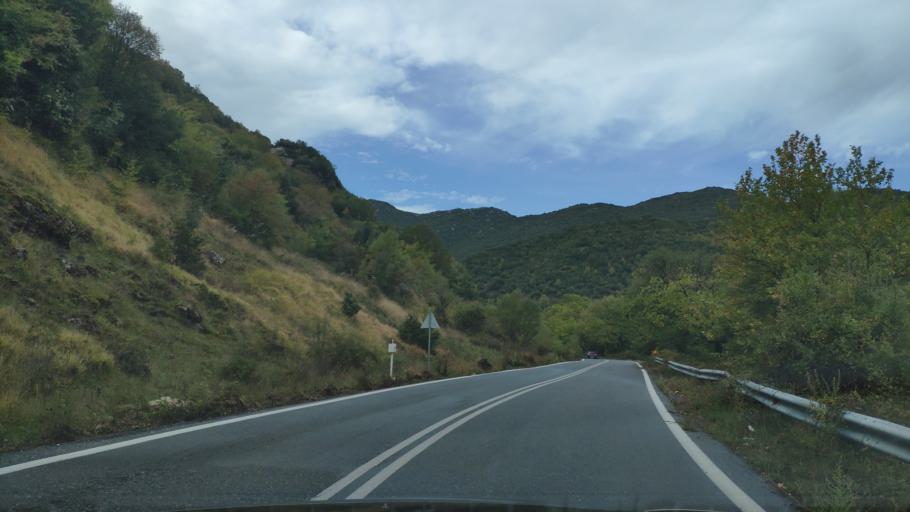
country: GR
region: Peloponnese
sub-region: Nomos Arkadias
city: Dimitsana
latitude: 37.6216
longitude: 22.0498
